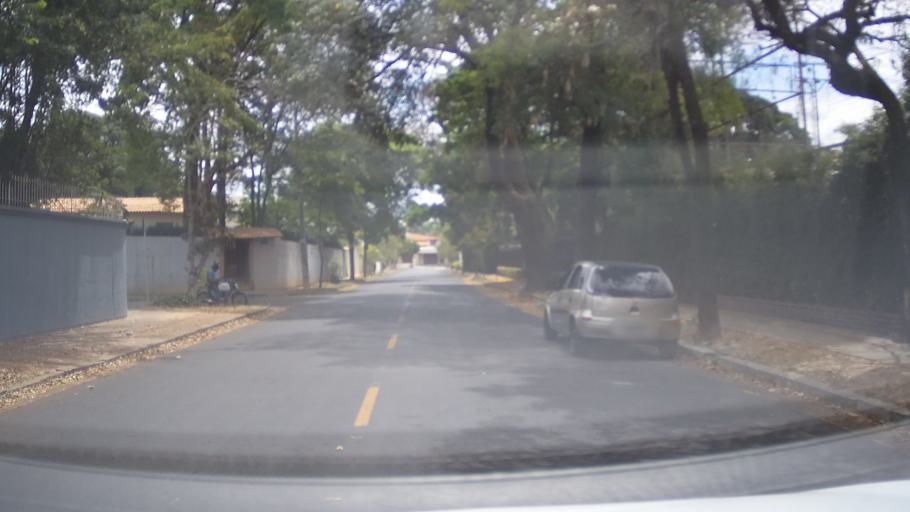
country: BR
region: Minas Gerais
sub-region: Belo Horizonte
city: Belo Horizonte
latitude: -19.8560
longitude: -43.9738
